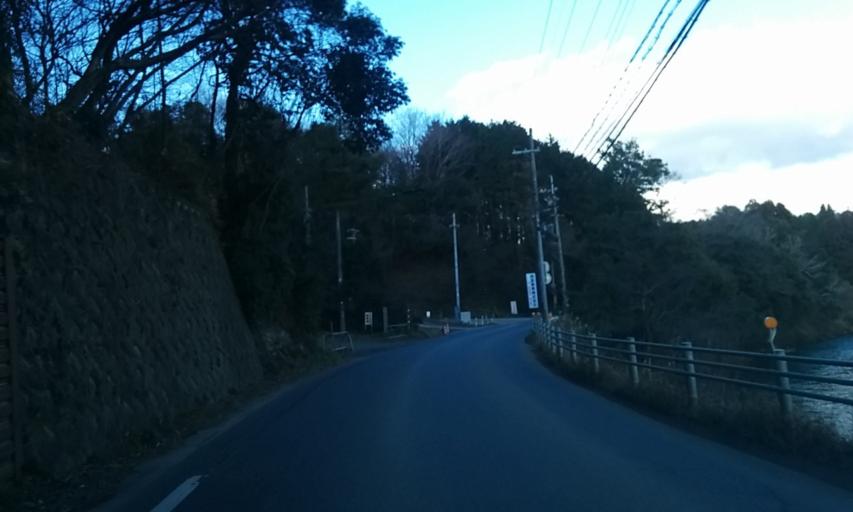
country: JP
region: Kyoto
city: Fukuchiyama
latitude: 35.3069
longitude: 135.1468
